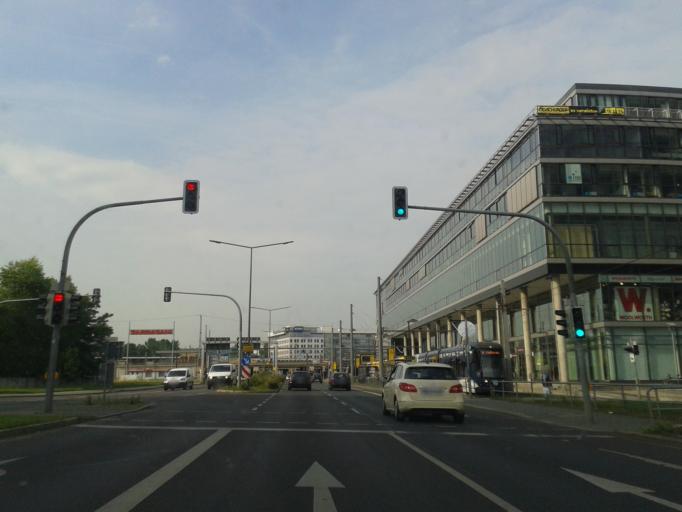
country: DE
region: Saxony
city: Dresden
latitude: 51.0421
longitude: 13.7360
